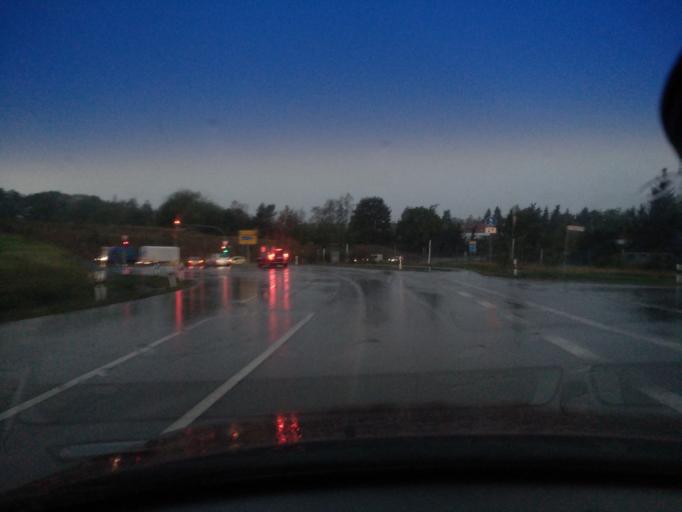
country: DE
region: Saxony
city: Bautzen
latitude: 51.1848
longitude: 14.4117
